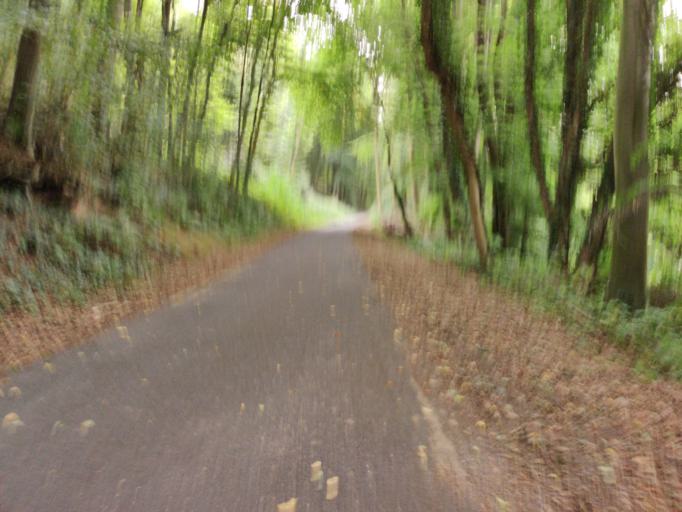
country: DE
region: Lower Saxony
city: Heyen
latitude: 51.9958
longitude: 9.5078
